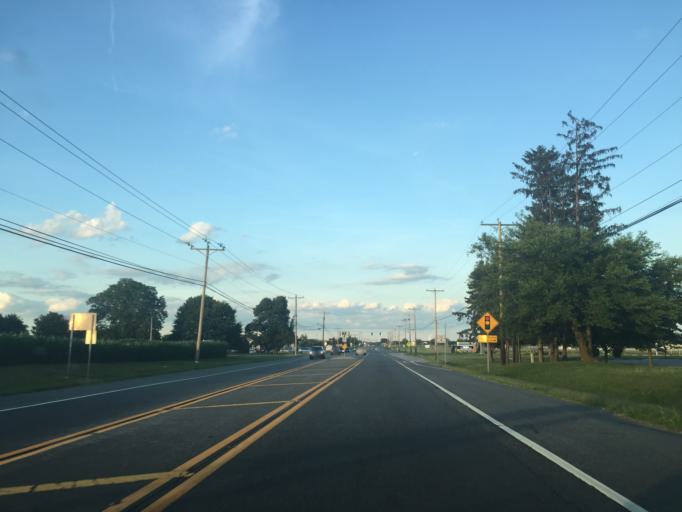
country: US
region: Delaware
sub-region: New Castle County
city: Middletown
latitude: 39.4513
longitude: -75.6934
